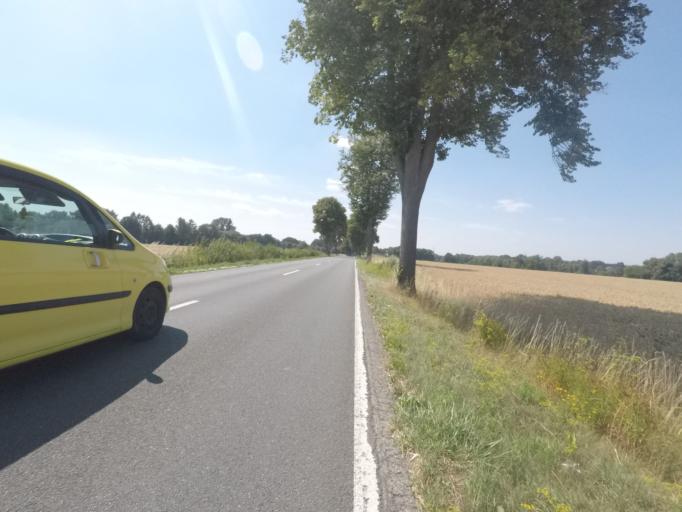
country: DE
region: North Rhine-Westphalia
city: Enger
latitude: 52.1117
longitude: 8.6019
